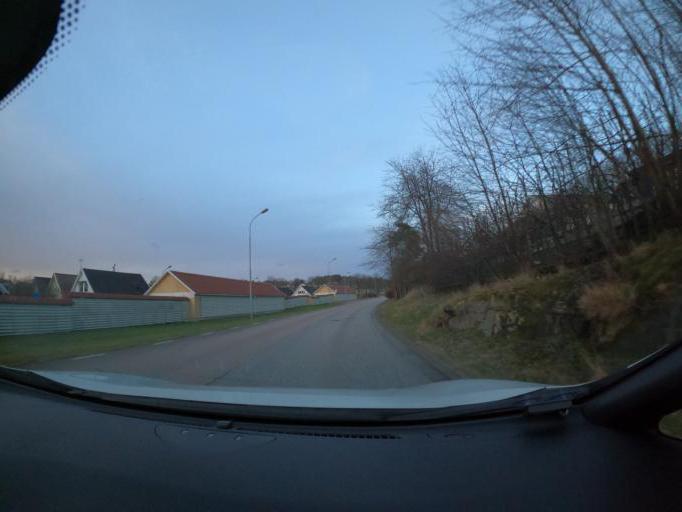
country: SE
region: Vaestra Goetaland
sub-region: Harryda Kommun
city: Molnlycke
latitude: 57.6462
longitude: 12.1215
